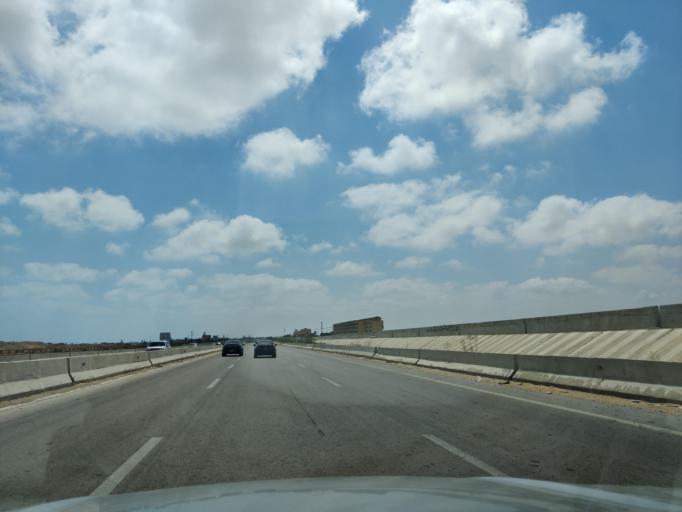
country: EG
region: Muhafazat Matruh
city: Al `Alamayn
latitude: 30.8212
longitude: 29.0089
